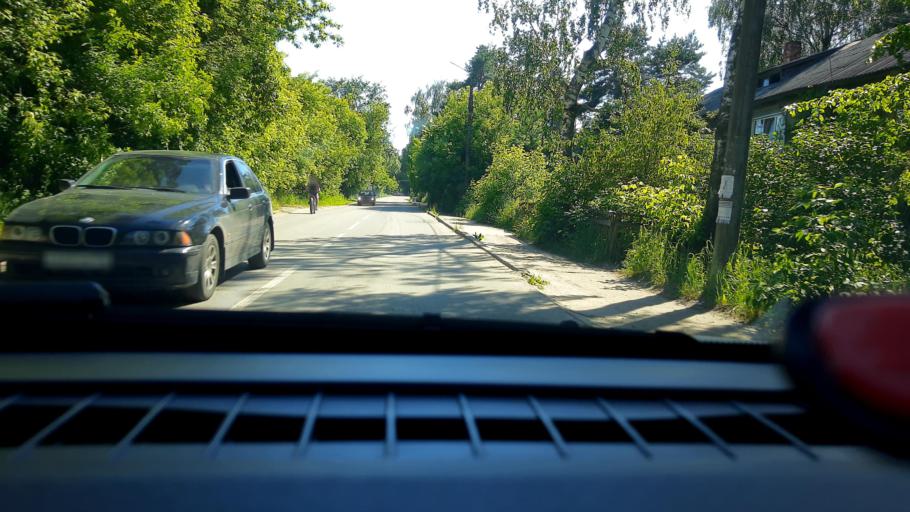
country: RU
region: Nizjnij Novgorod
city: Gidrotorf
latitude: 56.5243
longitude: 43.5483
